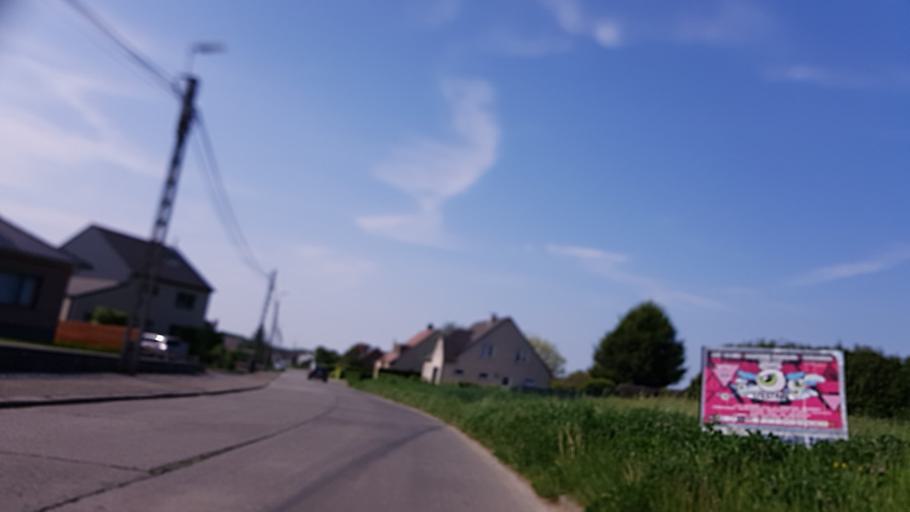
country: BE
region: Flanders
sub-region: Provincie Vlaams-Brabant
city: Tervuren
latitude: 50.8094
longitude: 4.5480
